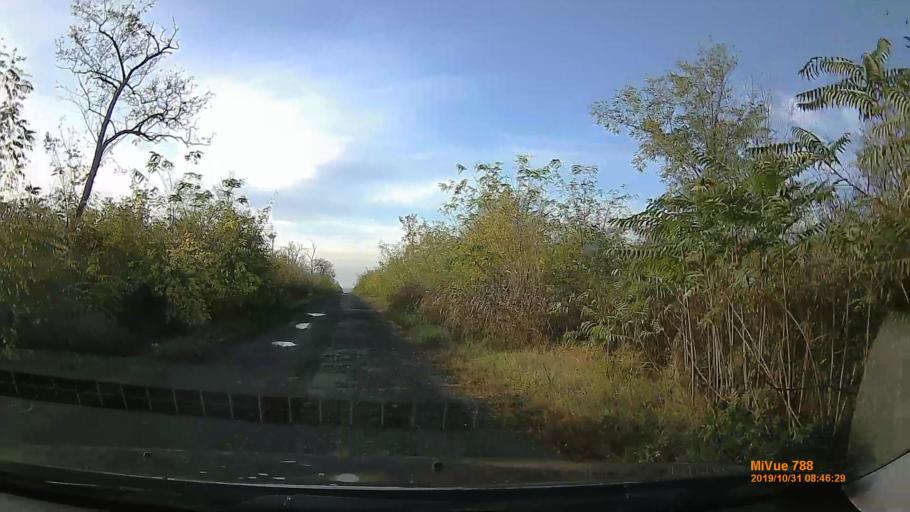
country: HU
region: Pest
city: Albertirsa
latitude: 47.2846
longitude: 19.6107
